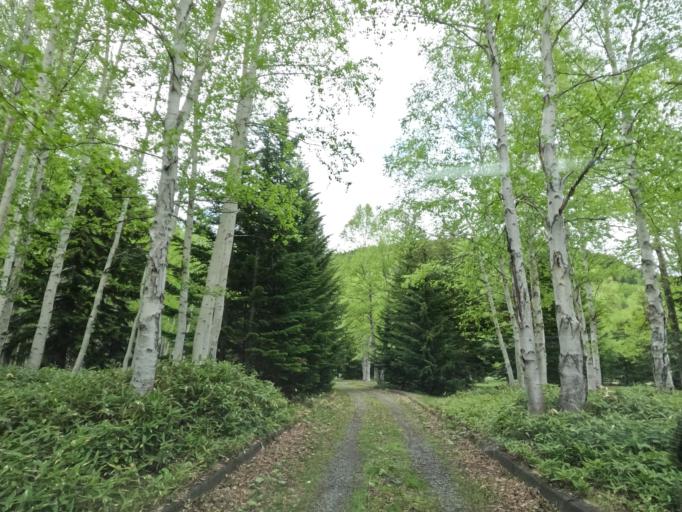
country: JP
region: Hokkaido
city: Kamikawa
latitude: 43.6433
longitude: 143.0224
